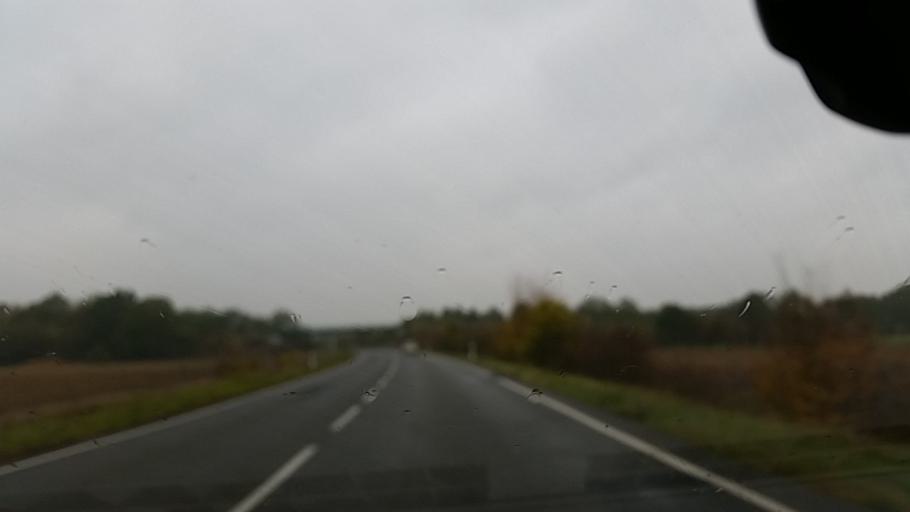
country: DE
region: Lower Saxony
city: Handorf
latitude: 53.3219
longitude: 10.3407
